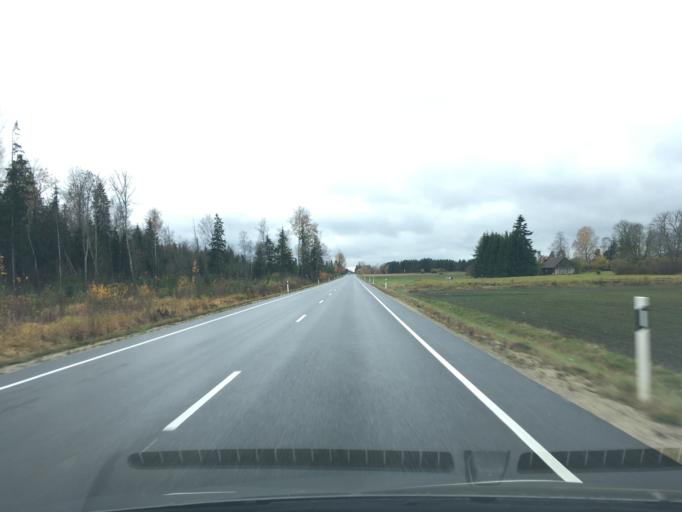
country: EE
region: Jogevamaa
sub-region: Tabivere vald
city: Tabivere
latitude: 58.4505
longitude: 26.5210
